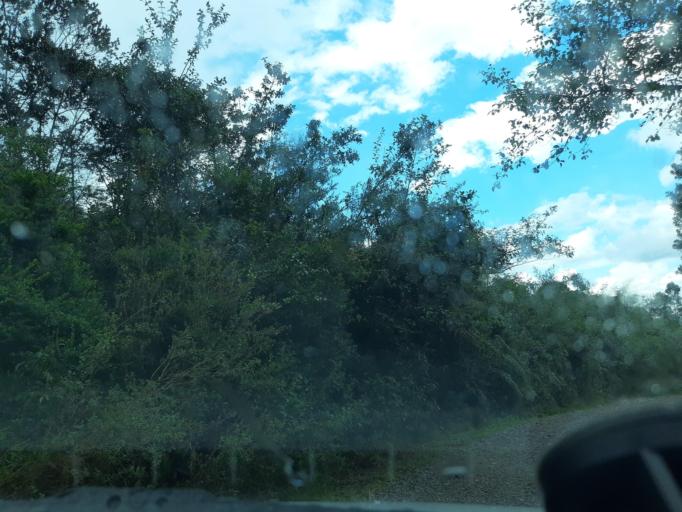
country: CO
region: Boyaca
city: Raquira
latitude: 5.5077
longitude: -73.6874
